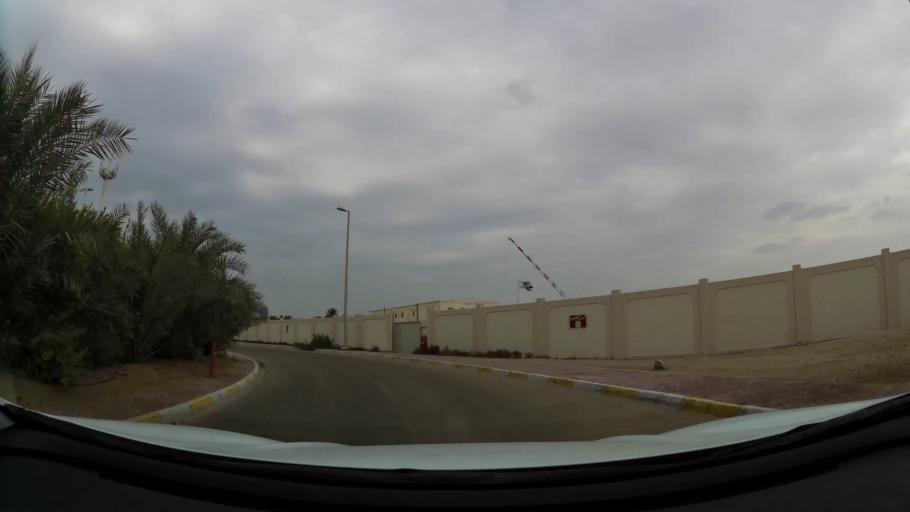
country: AE
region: Abu Dhabi
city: Abu Dhabi
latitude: 24.4351
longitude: 54.3856
